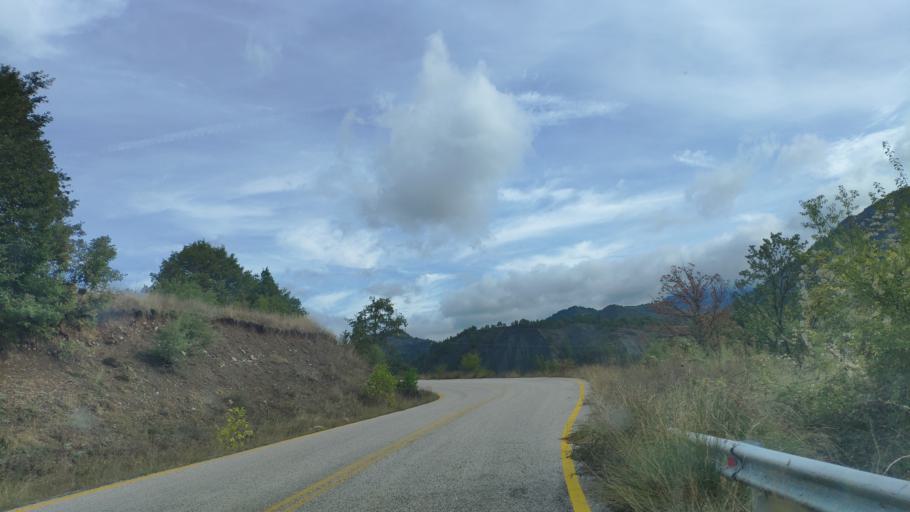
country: GR
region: West Macedonia
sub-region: Nomos Kastorias
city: Nestorio
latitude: 40.2437
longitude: 20.9886
